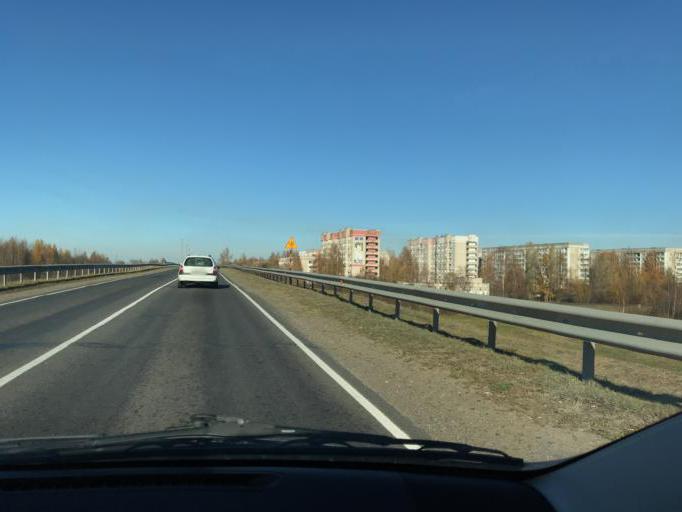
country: BY
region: Vitebsk
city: Polatsk
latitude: 55.4627
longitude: 28.7598
